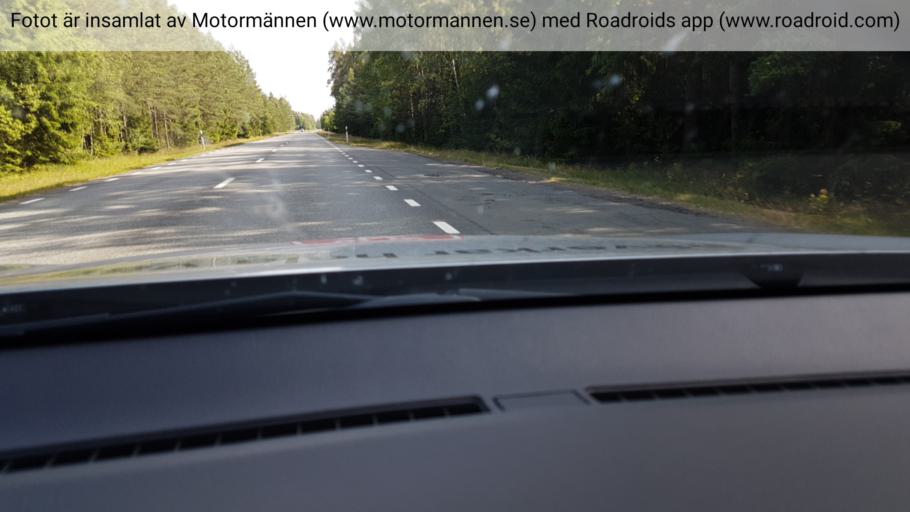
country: SE
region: Joenkoeping
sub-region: Eksjo Kommun
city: Eksjoe
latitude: 57.6244
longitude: 14.9696
